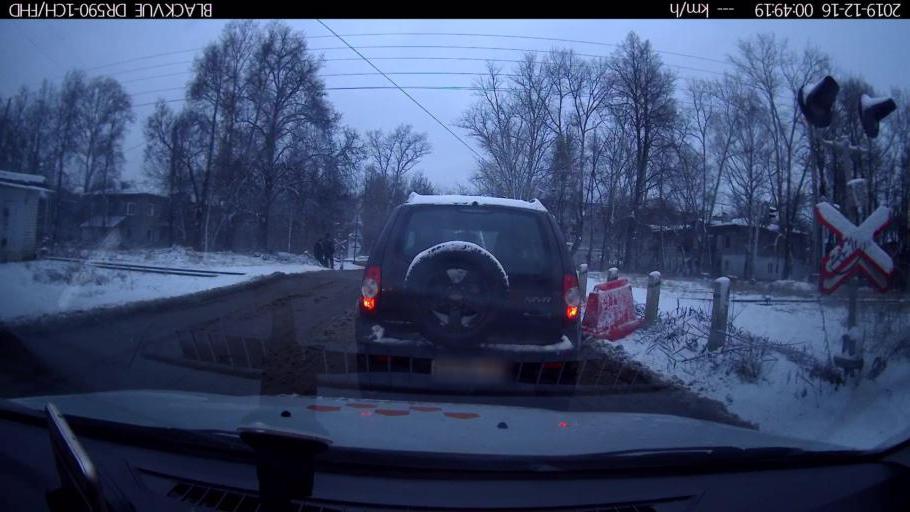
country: RU
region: Nizjnij Novgorod
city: Gorbatovka
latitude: 56.3114
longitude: 43.8583
